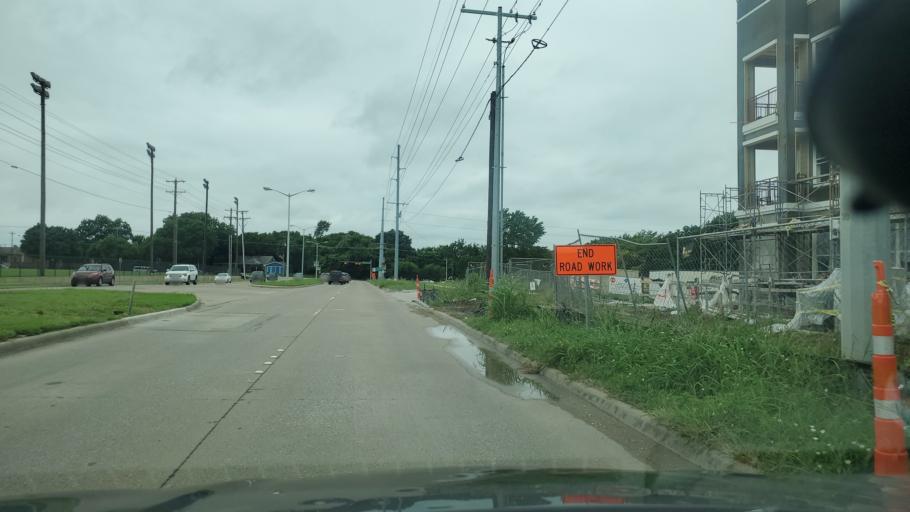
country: US
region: Texas
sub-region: Dallas County
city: Garland
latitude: 32.9552
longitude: -96.6549
